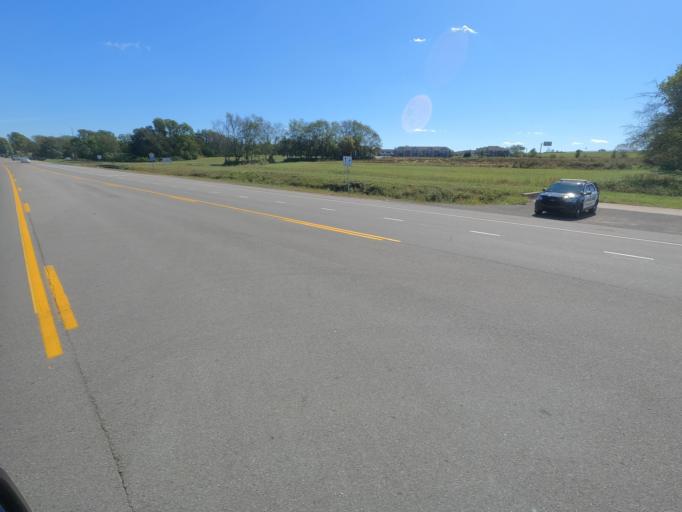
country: US
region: Tennessee
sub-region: Sumner County
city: Gallatin
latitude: 36.3879
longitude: -86.4726
